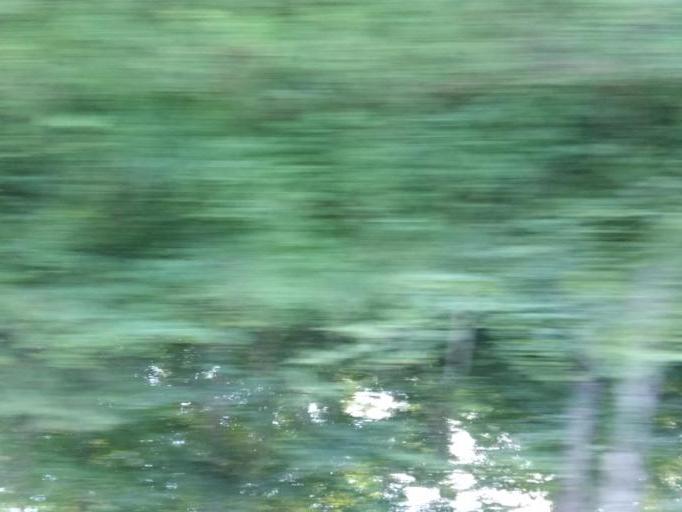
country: US
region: Tennessee
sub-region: Blount County
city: Eagleton Village
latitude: 35.8220
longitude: -83.9241
